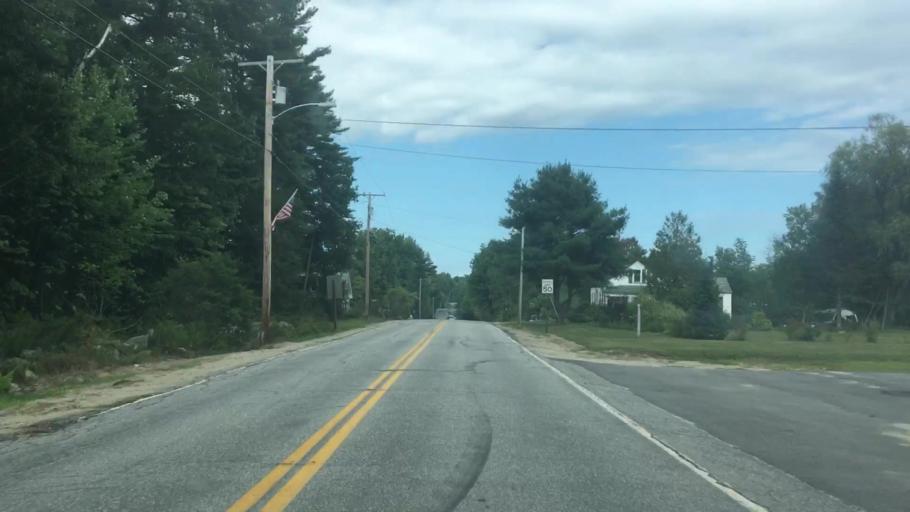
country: US
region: Maine
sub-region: Oxford County
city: Oxford
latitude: 44.0600
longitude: -70.5523
